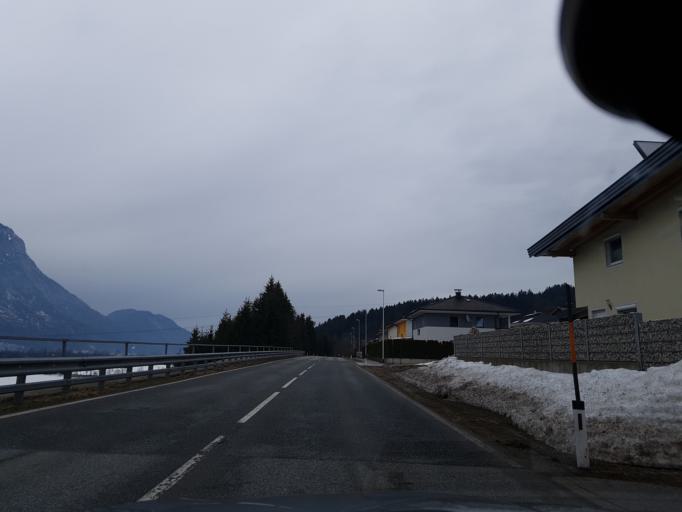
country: AT
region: Tyrol
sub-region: Politischer Bezirk Kufstein
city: Bad Haering
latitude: 47.5245
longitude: 12.1035
